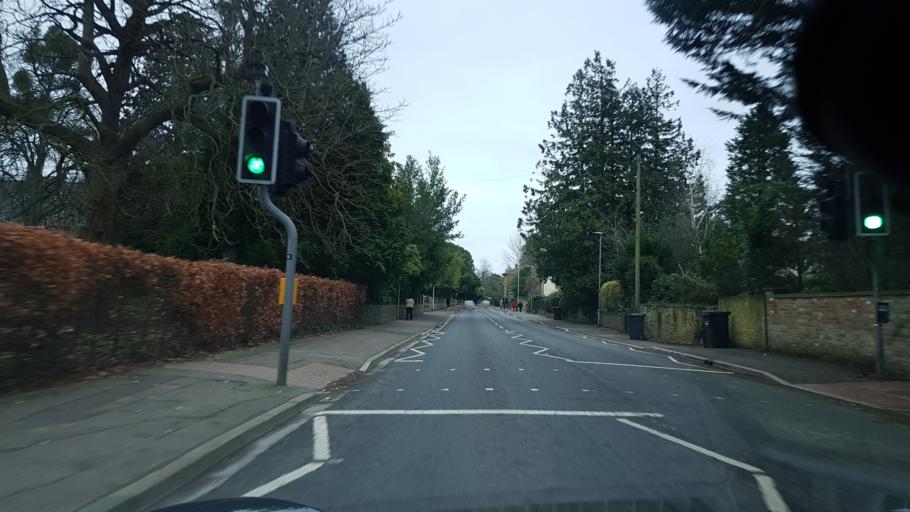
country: GB
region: England
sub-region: Somerset
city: Taunton
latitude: 51.0101
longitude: -3.0932
